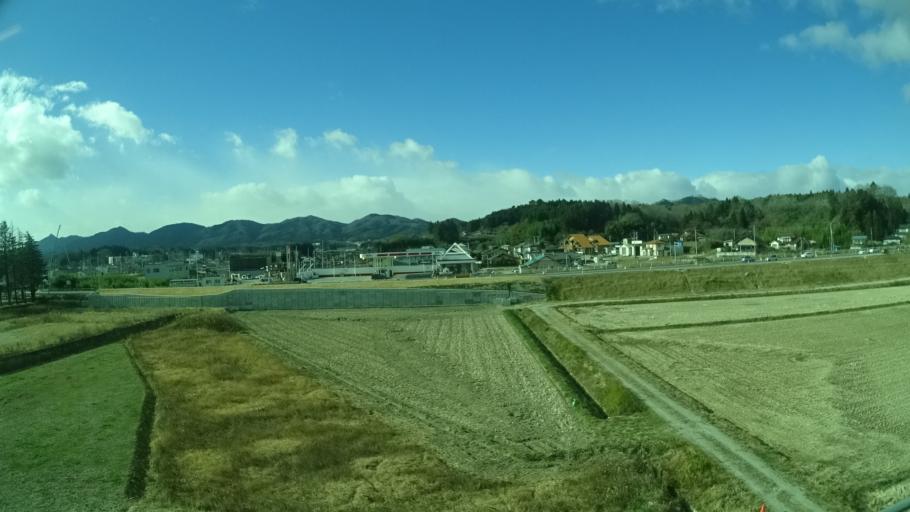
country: JP
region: Miyagi
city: Watari
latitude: 37.9264
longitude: 140.9000
